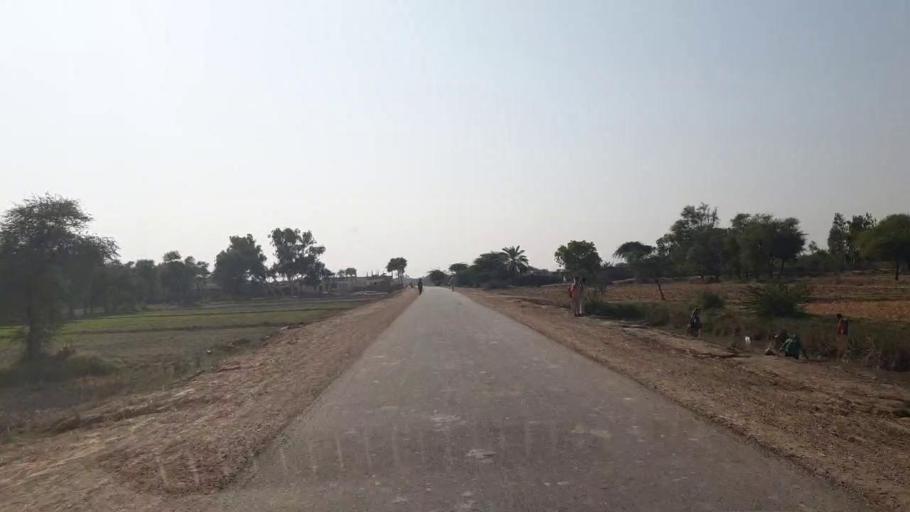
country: PK
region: Sindh
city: Matli
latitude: 24.9759
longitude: 68.6550
